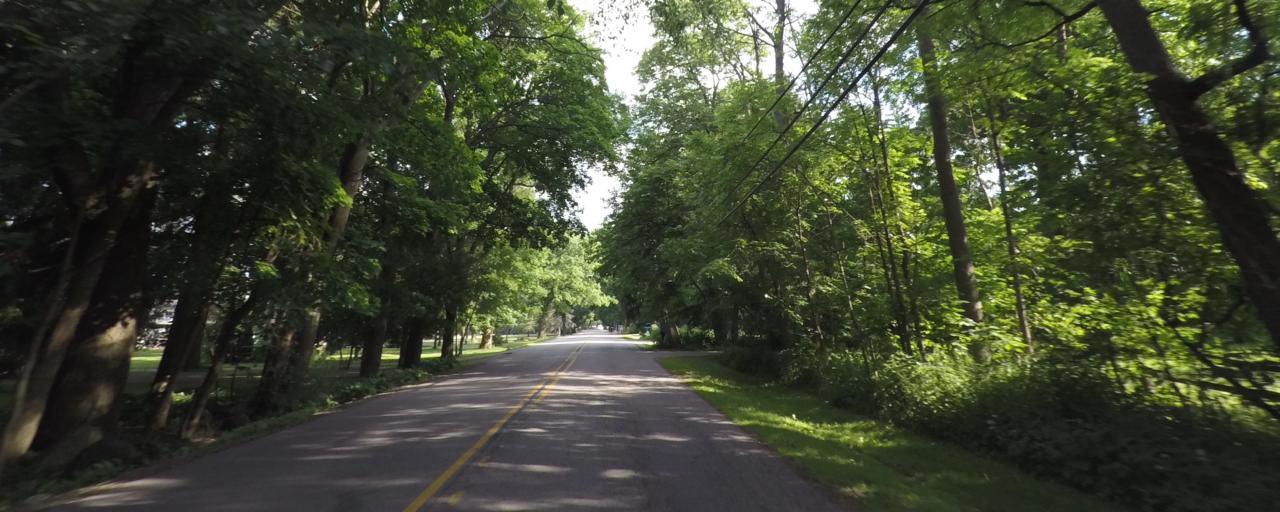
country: US
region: Wisconsin
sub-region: Milwaukee County
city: Hales Corners
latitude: 42.9427
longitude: -88.0284
